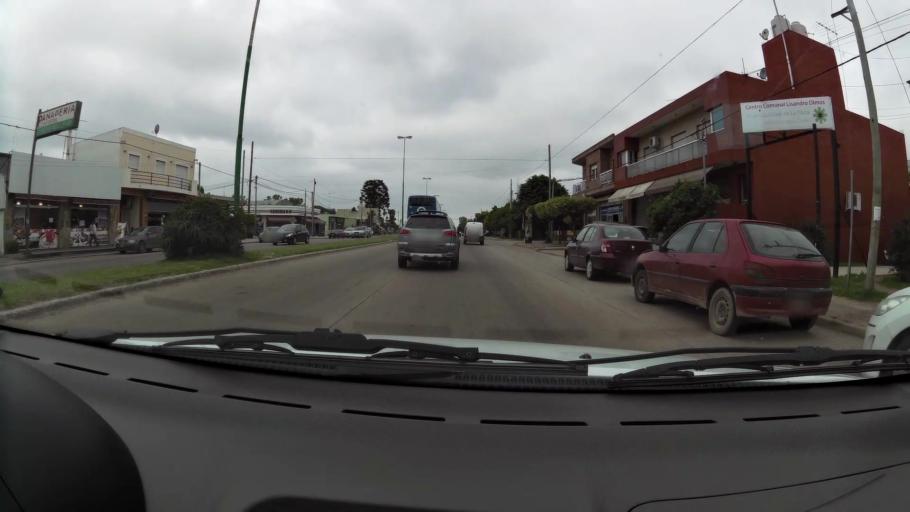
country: AR
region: Buenos Aires
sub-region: Partido de La Plata
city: La Plata
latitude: -34.9947
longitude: -58.0475
